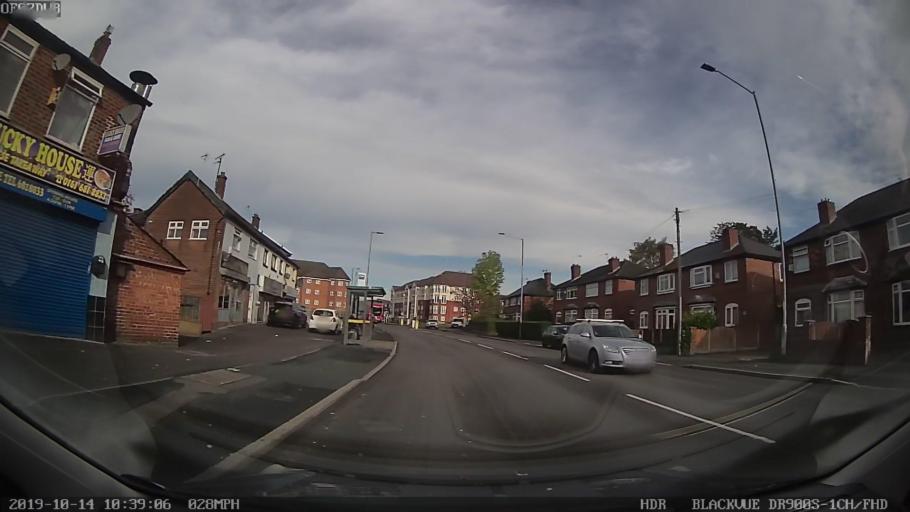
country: GB
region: England
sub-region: Manchester
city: Failsworth
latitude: 53.5218
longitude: -2.1823
